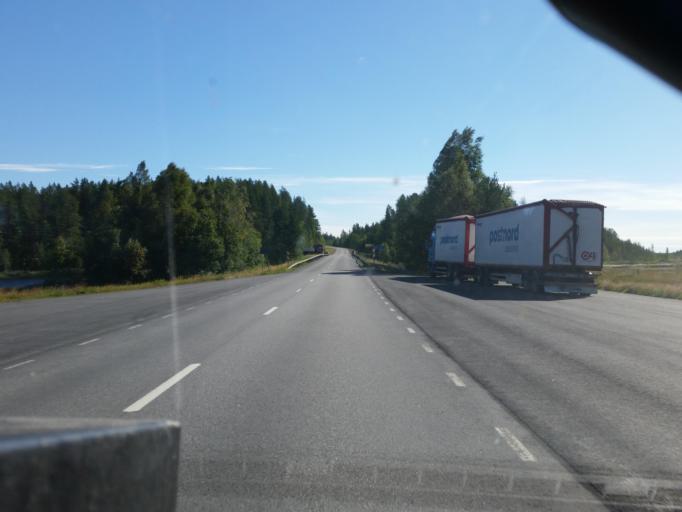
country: SE
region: Vaesterbotten
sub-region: Skelleftea Kommun
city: Storvik
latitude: 65.3291
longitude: 20.6111
